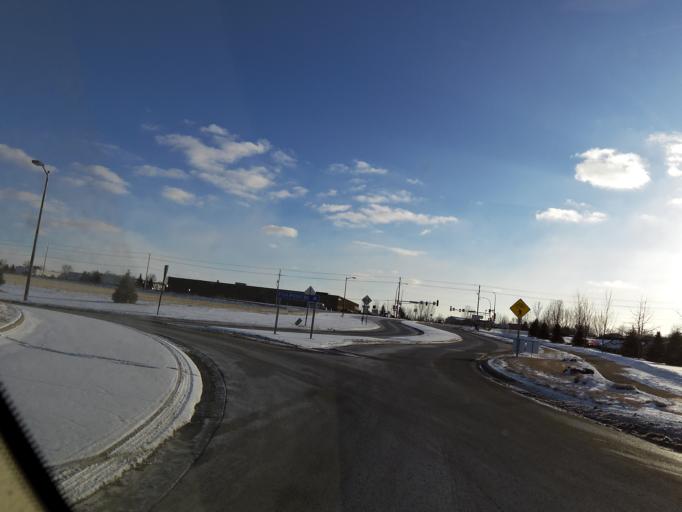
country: US
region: Minnesota
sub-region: Scott County
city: Prior Lake
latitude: 44.7087
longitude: -93.4107
